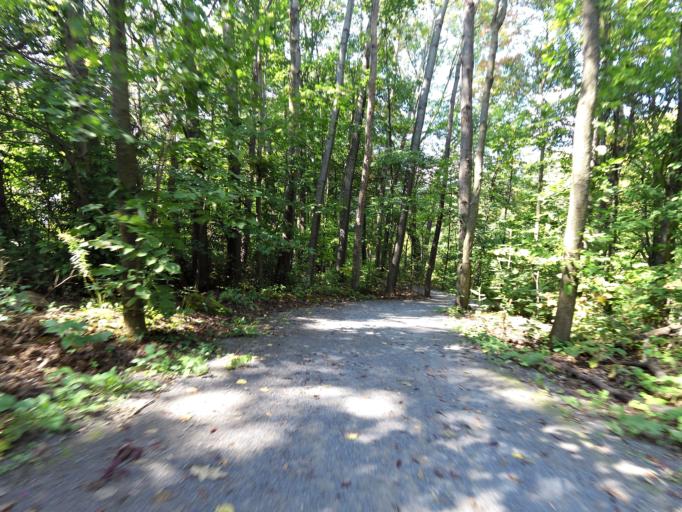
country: CA
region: Ontario
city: Bells Corners
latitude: 45.2597
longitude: -75.7103
